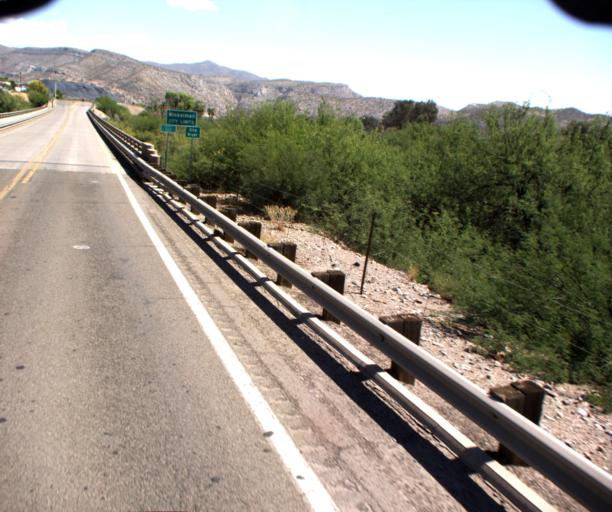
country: US
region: Arizona
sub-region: Pinal County
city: Kearny
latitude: 32.9842
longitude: -110.7696
